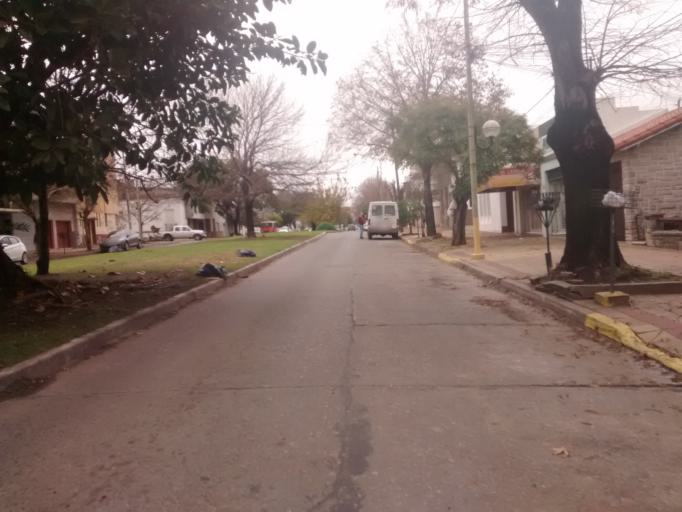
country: AR
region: Buenos Aires
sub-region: Partido de La Plata
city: La Plata
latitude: -34.8957
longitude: -57.9514
